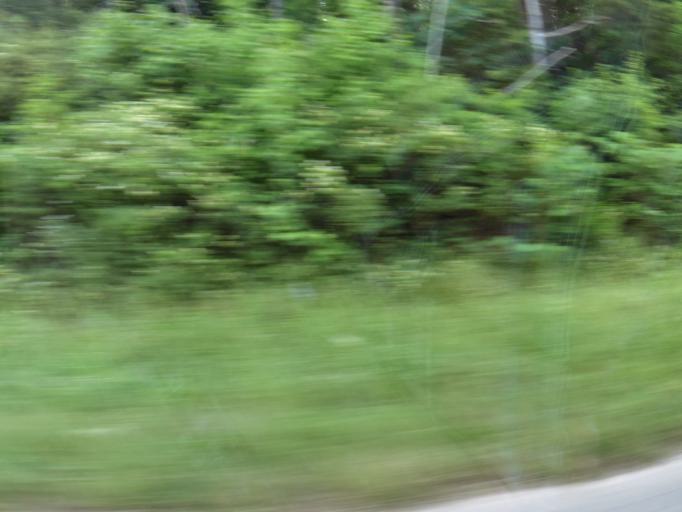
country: US
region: Tennessee
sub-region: Knox County
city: Knoxville
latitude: 35.8866
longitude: -83.9459
